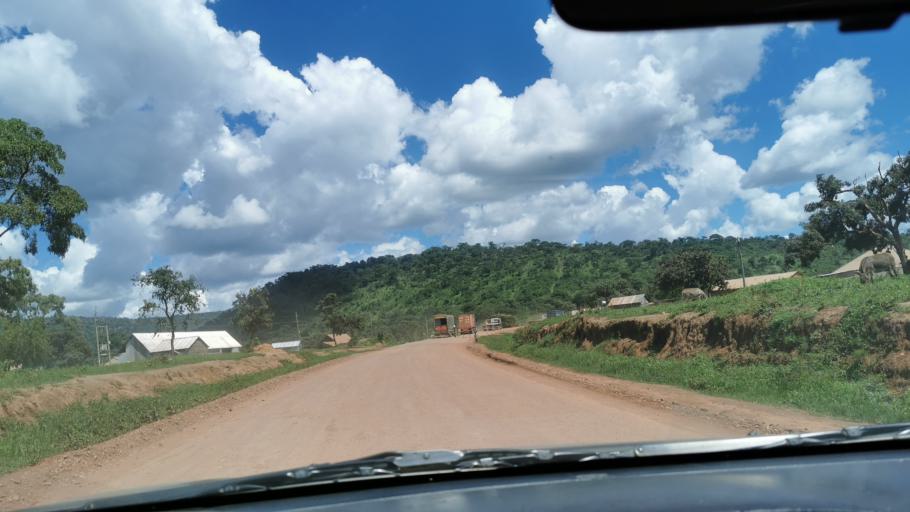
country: TZ
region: Kagera
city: Biharamulo
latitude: -2.8900
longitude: 31.1563
